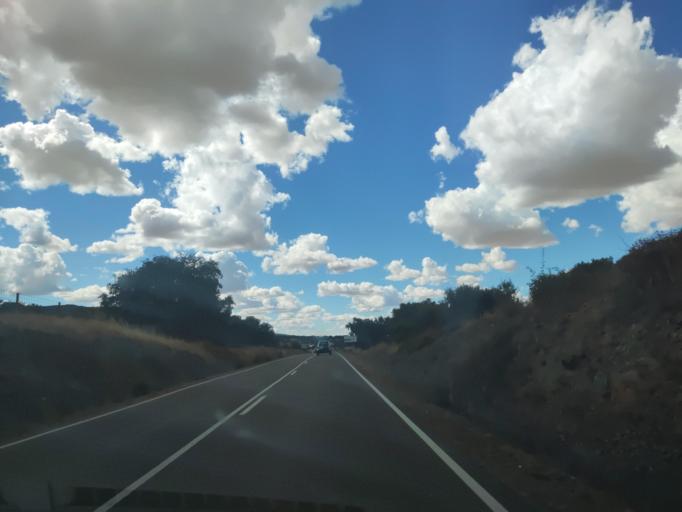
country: ES
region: Castille and Leon
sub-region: Provincia de Salamanca
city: Tejeda y Segoyuela
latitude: 40.6402
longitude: -6.0553
